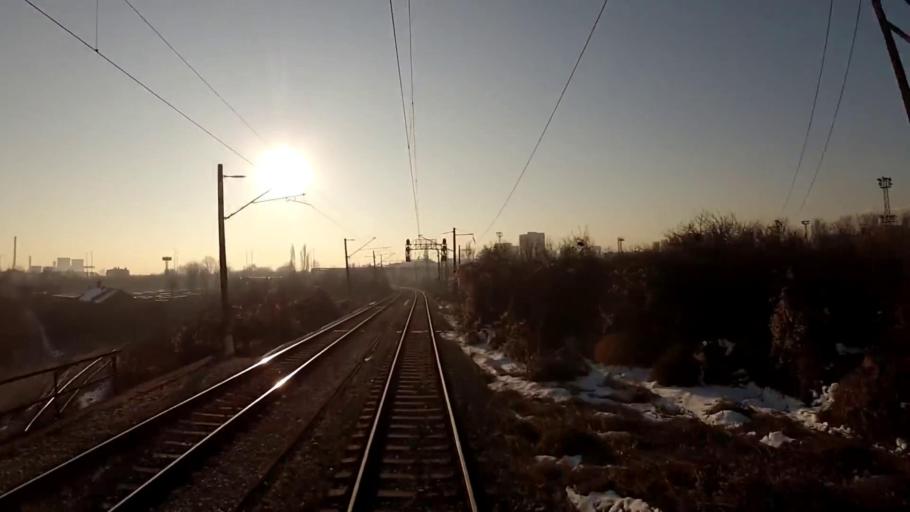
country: BG
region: Sofia-Capital
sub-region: Stolichna Obshtina
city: Sofia
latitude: 42.7256
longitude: 23.2881
